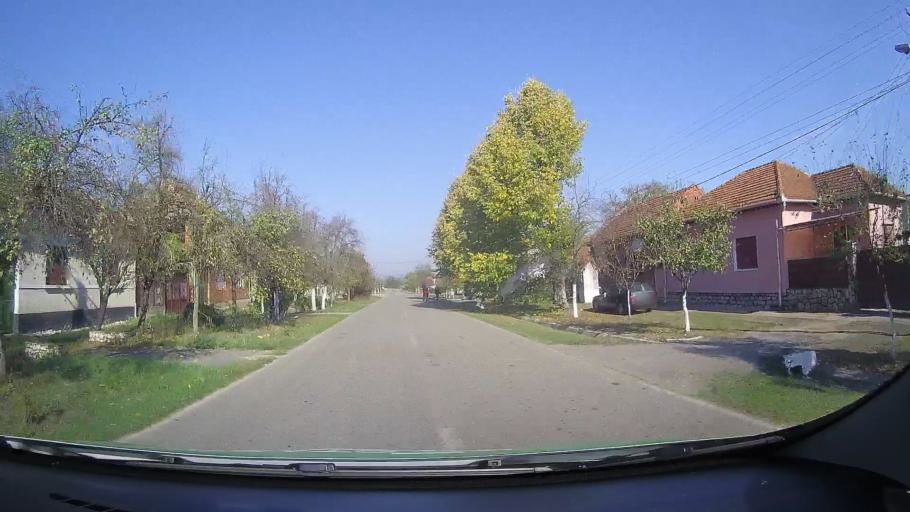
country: RO
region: Timis
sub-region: Comuna Curtea
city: Curtea
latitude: 45.8305
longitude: 22.3071
